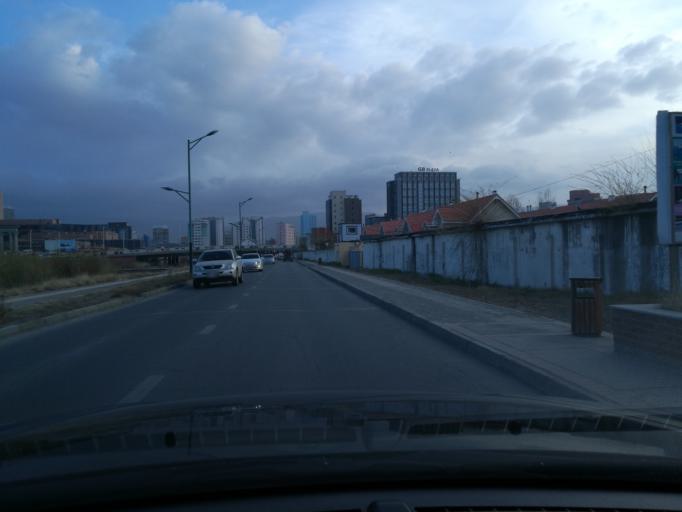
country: MN
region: Ulaanbaatar
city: Ulaanbaatar
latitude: 47.9252
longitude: 106.9313
